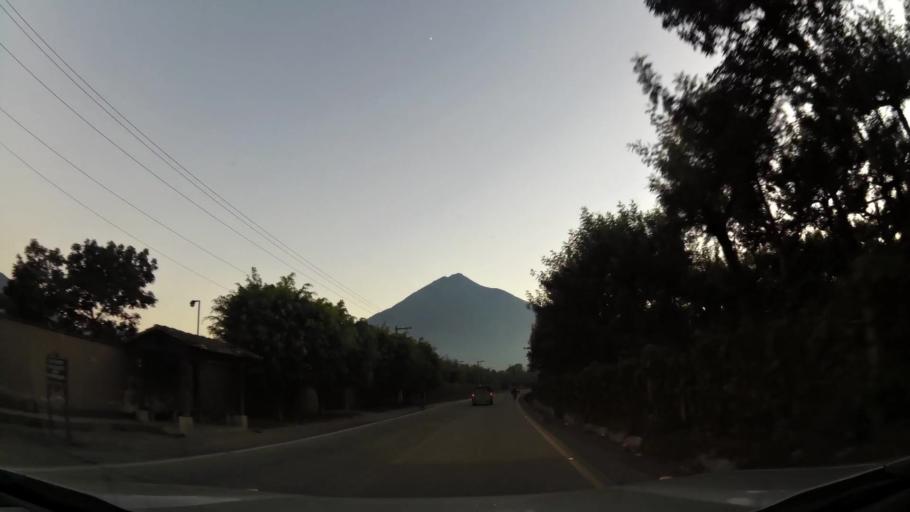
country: GT
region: Sacatepequez
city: Ciudad Vieja
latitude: 14.5426
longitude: -90.7467
